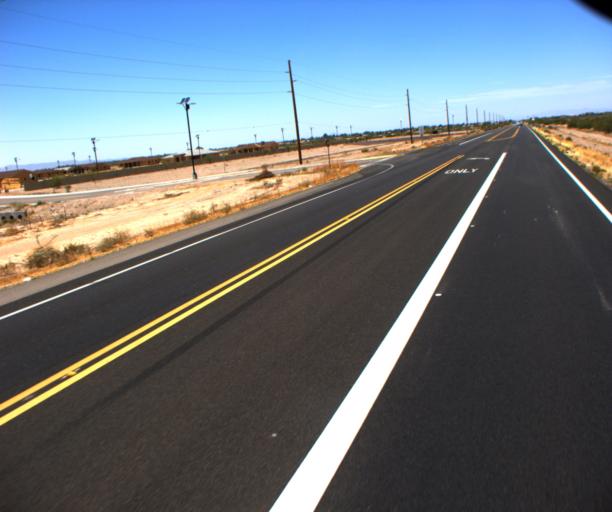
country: US
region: Arizona
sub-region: Maricopa County
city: Sun Lakes
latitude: 33.1839
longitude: -111.8409
